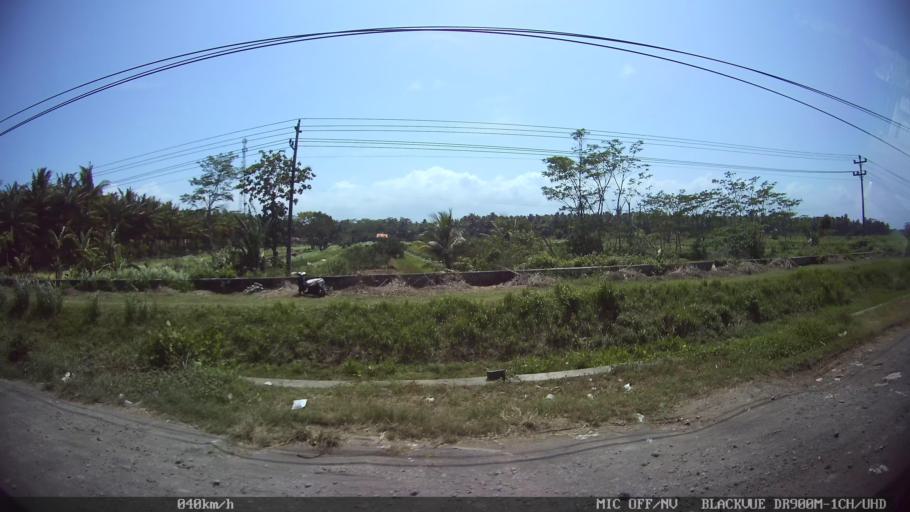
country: ID
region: Daerah Istimewa Yogyakarta
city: Srandakan
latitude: -7.9285
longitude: 110.1337
